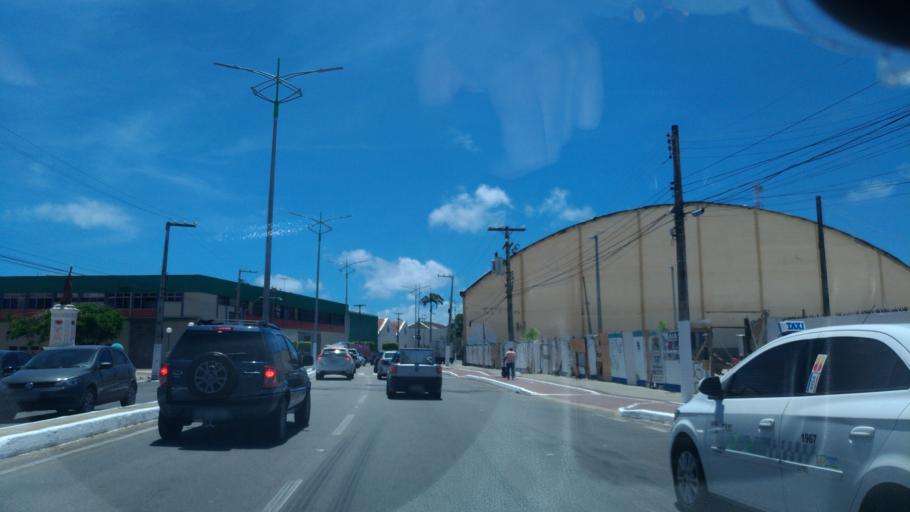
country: BR
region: Alagoas
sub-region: Maceio
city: Maceio
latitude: -9.6729
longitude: -35.7229
